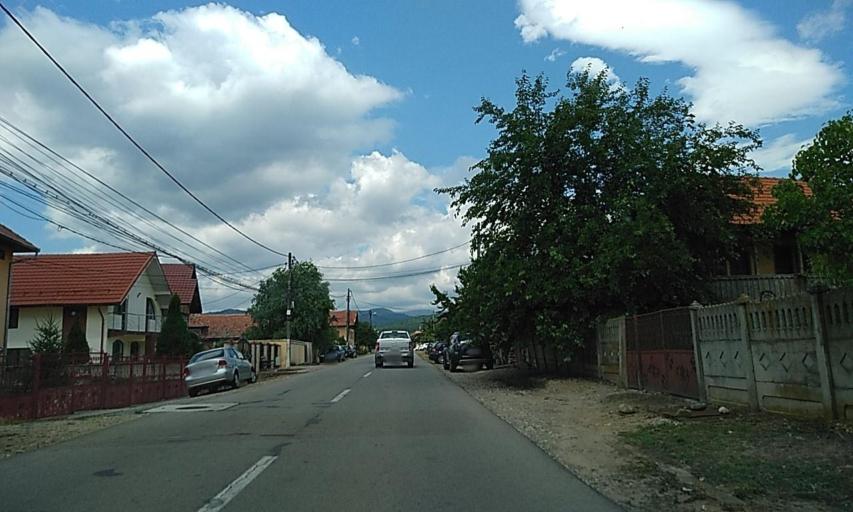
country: RO
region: Gorj
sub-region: Comuna Bumbesti-Jiu
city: Bumbesti-Jiu
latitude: 45.1485
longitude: 23.3928
